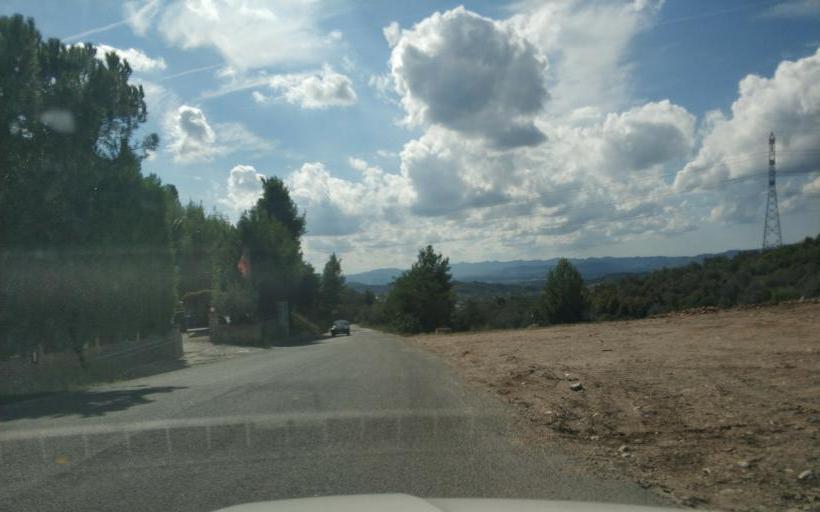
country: AL
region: Durres
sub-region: Rrethi i Krujes
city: Kruje
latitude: 41.4877
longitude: 19.7675
